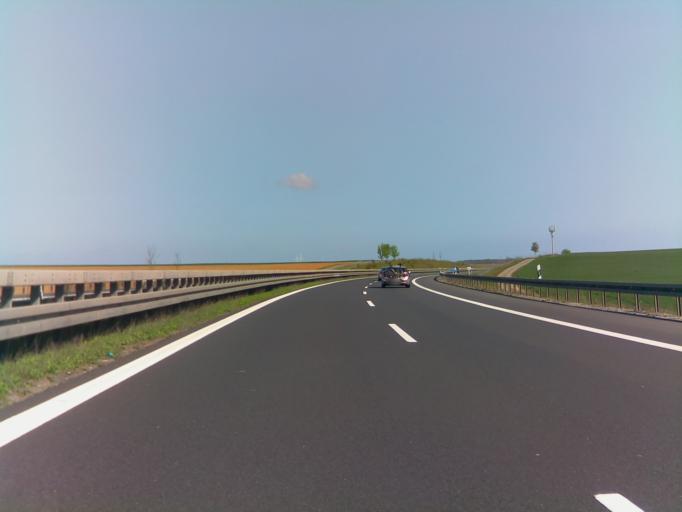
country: DE
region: Bavaria
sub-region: Regierungsbezirk Unterfranken
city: Geldersheim
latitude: 50.0347
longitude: 10.1374
